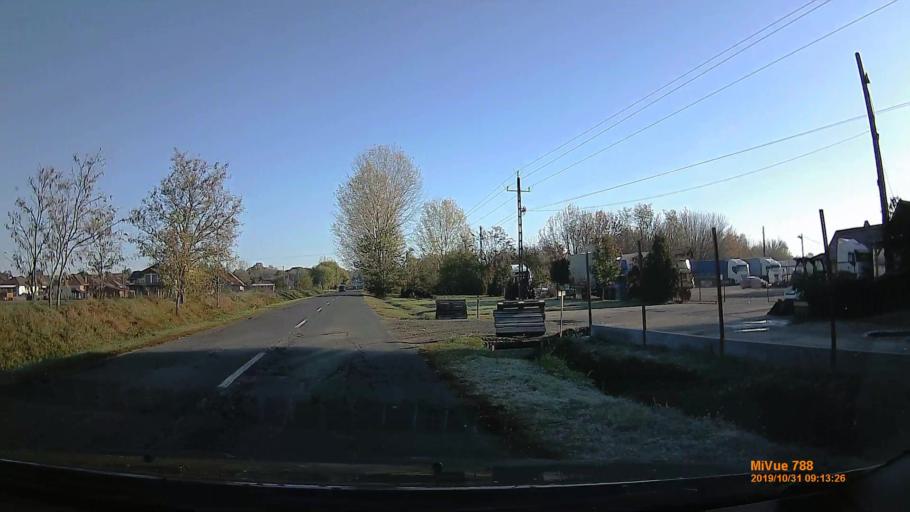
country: HU
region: Pest
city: Peteri
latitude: 47.3820
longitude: 19.4066
